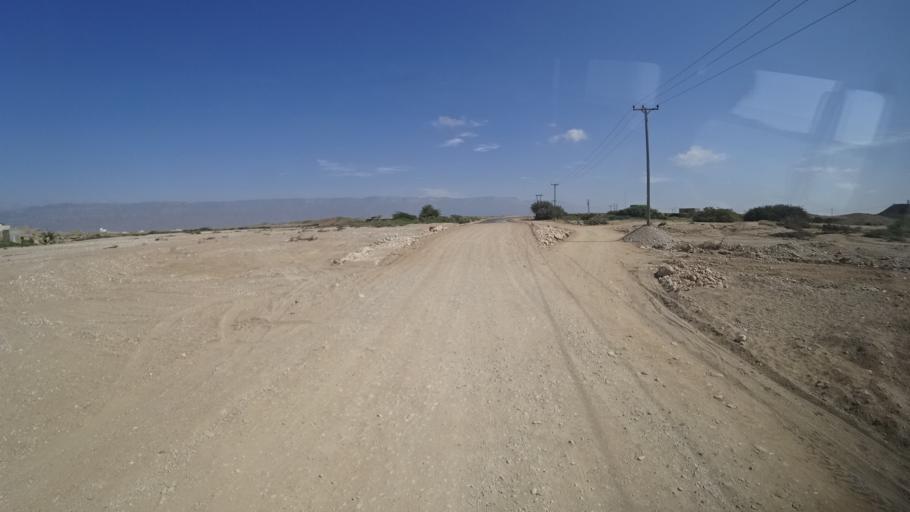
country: OM
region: Zufar
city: Salalah
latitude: 16.9634
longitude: 54.7467
